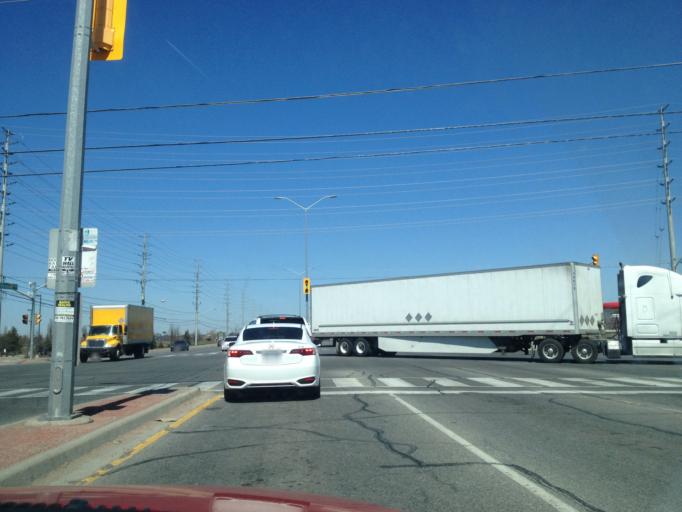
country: CA
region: Ontario
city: Brampton
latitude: 43.6860
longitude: -79.8088
